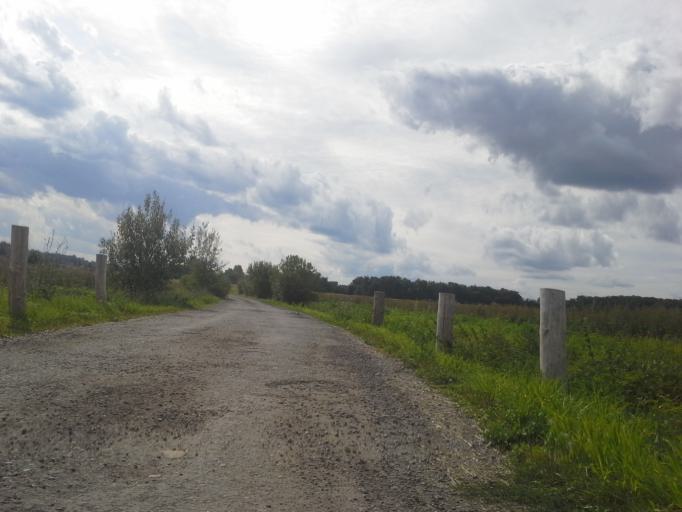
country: RU
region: Moskovskaya
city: Filimonki
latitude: 55.5339
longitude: 37.3737
